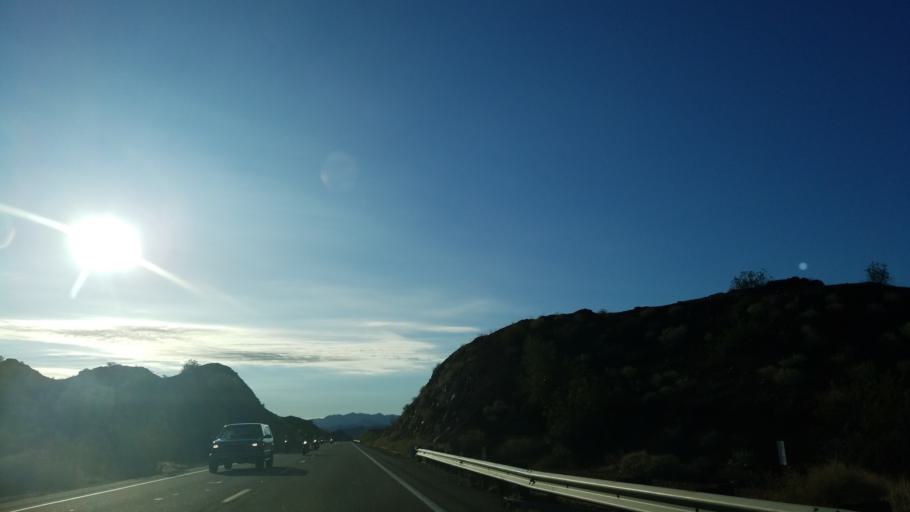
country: US
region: Arizona
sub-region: La Paz County
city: Cienega Springs
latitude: 34.3161
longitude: -114.1125
